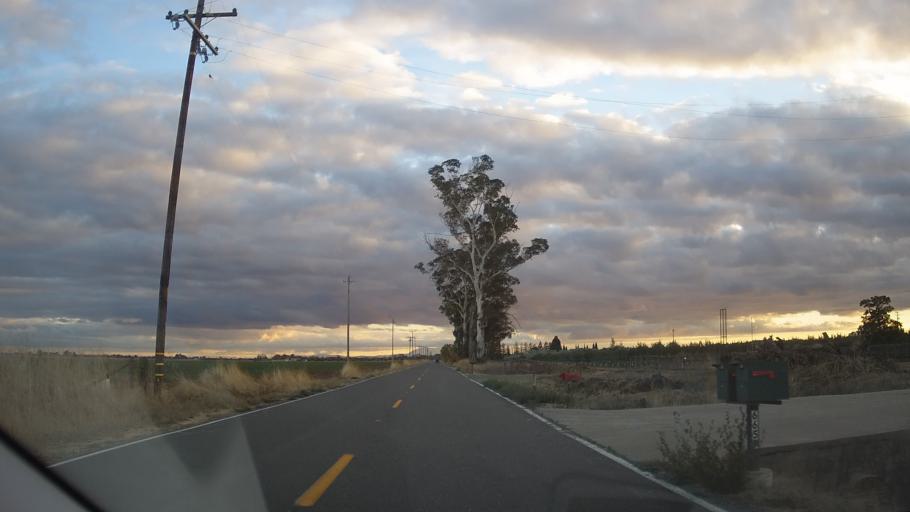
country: US
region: California
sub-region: Solano County
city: Hartley
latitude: 38.3809
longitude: -121.9059
